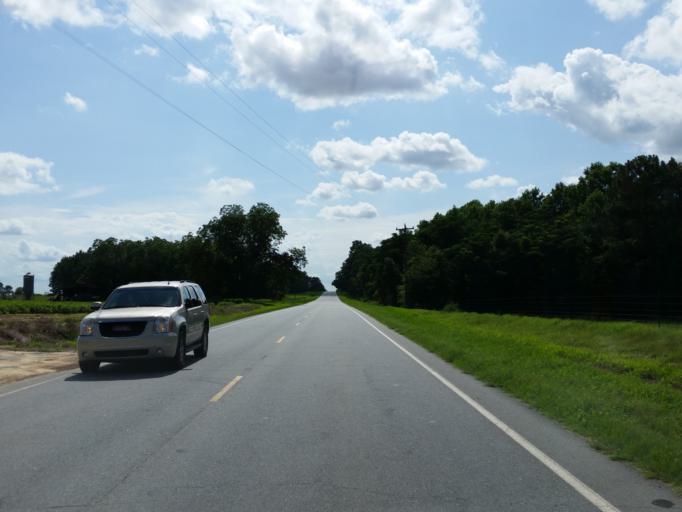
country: US
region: Georgia
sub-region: Turner County
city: Ashburn
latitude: 31.6588
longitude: -83.5719
